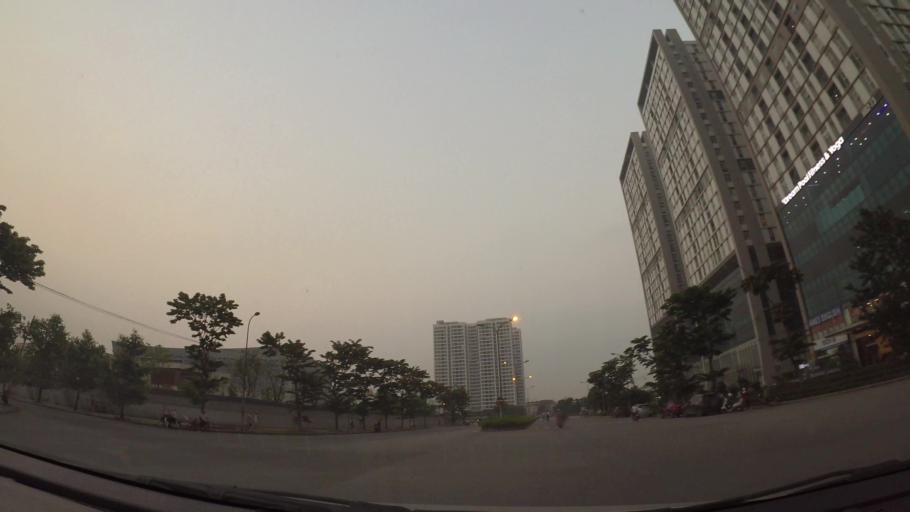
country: VN
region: Ha Noi
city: Tay Ho
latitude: 21.0659
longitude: 105.7977
